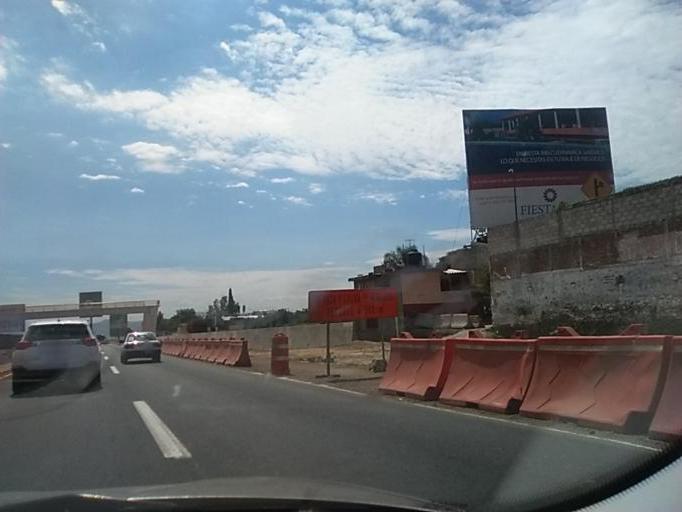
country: MX
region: Morelos
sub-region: Cuernavaca
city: Colonia los Cerritos
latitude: 18.9503
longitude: -99.1895
